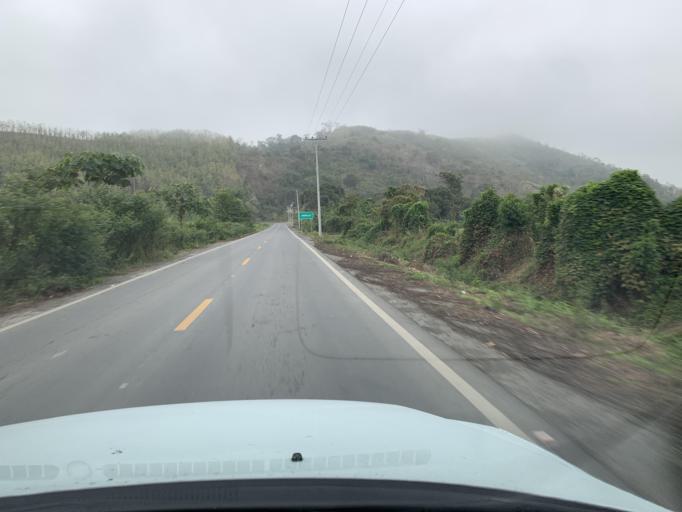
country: EC
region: Guayas
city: Coronel Marcelino Mariduena
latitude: -2.3514
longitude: -79.5294
